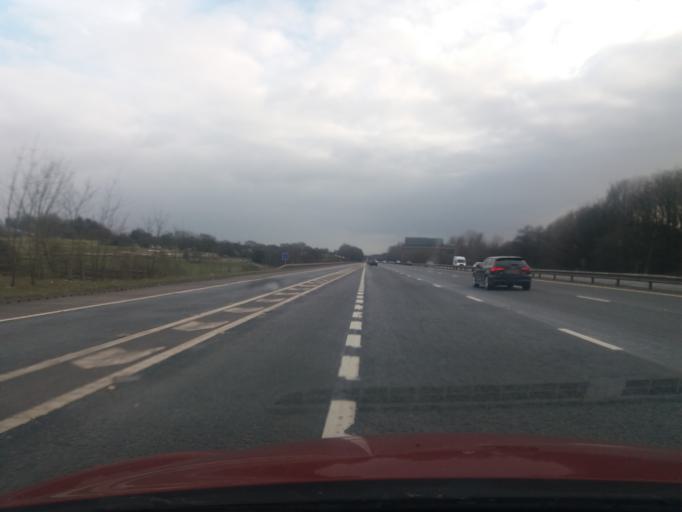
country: GB
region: England
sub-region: Lancashire
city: Clayton-le-Woods
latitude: 53.7130
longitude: -2.6304
